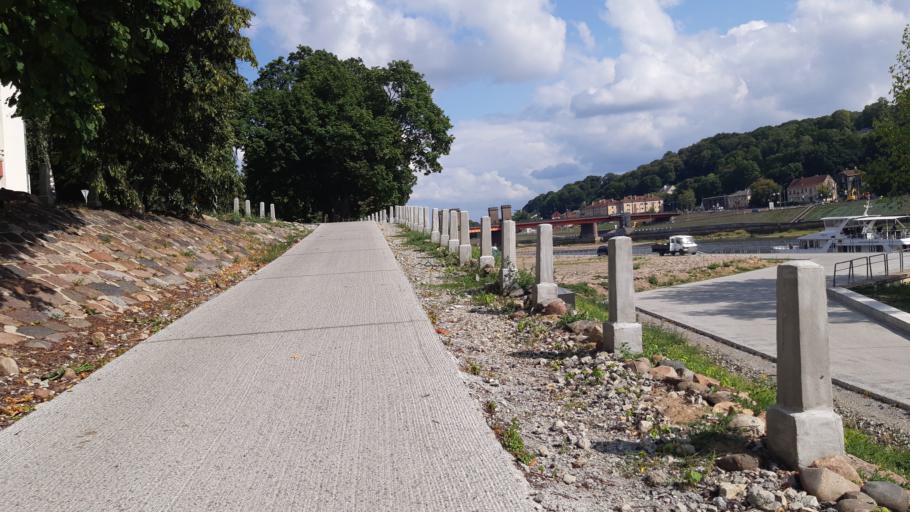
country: LT
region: Kauno apskritis
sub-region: Kaunas
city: Kaunas
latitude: 54.8953
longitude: 23.8824
